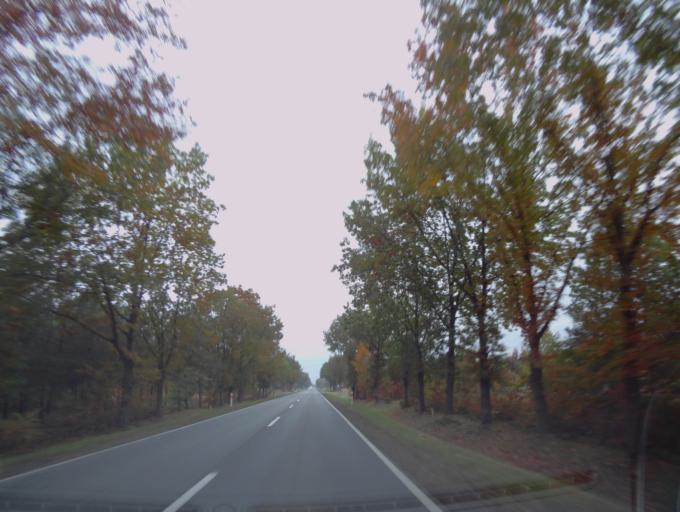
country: PL
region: Subcarpathian Voivodeship
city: Nowa Sarzyna
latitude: 50.3407
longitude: 22.3290
